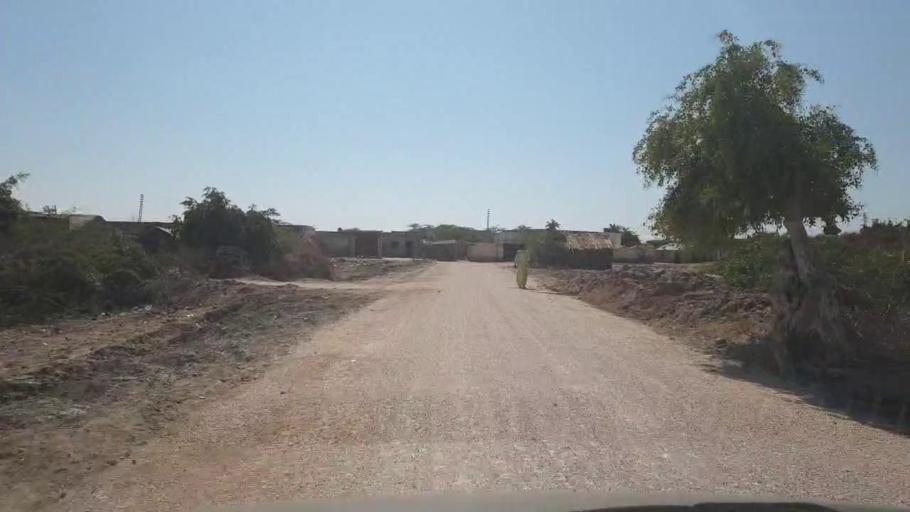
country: PK
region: Sindh
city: Dhoro Naro
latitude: 25.4511
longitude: 69.6007
